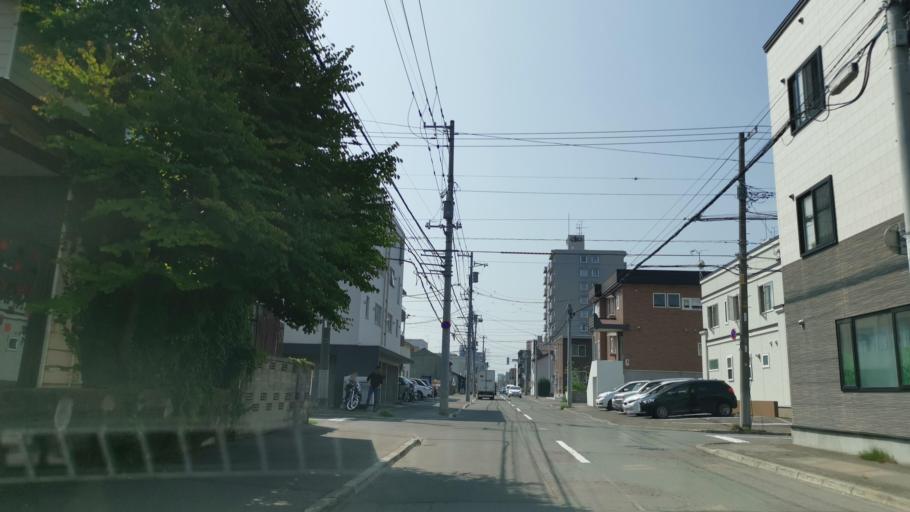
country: JP
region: Hokkaido
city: Sapporo
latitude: 43.0424
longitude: 141.3489
